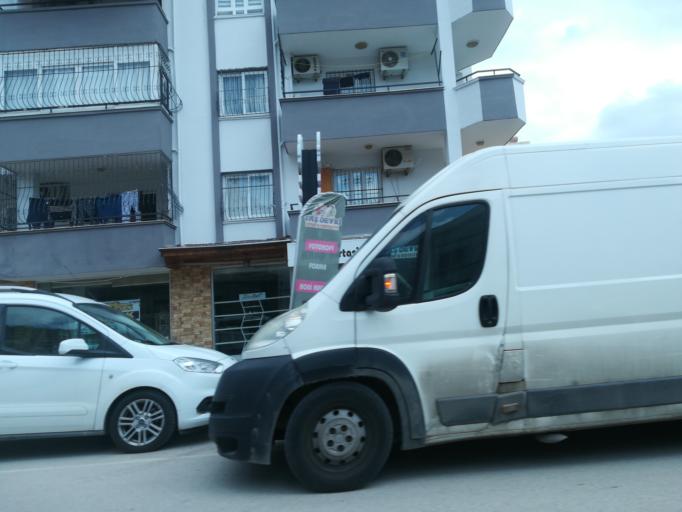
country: TR
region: Adana
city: Adana
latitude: 37.0396
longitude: 35.3130
